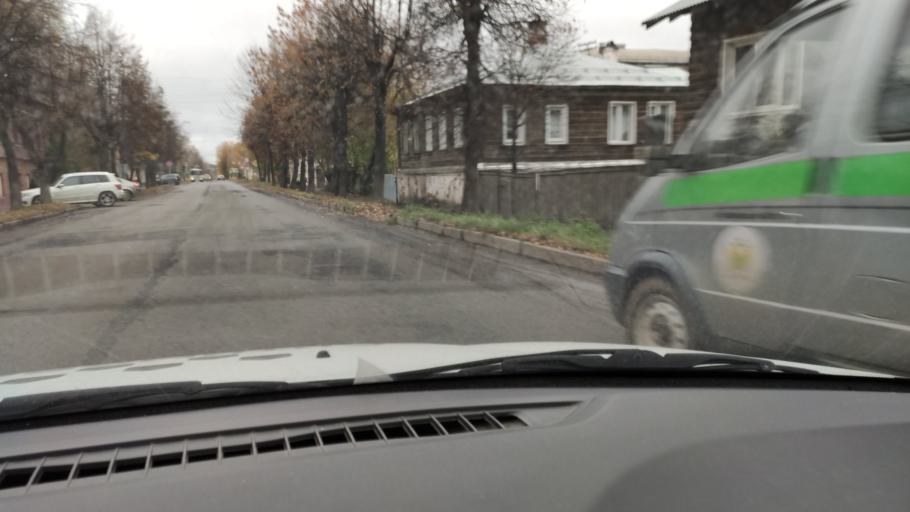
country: RU
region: Kirov
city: Slobodskoy
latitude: 58.7344
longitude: 50.1827
